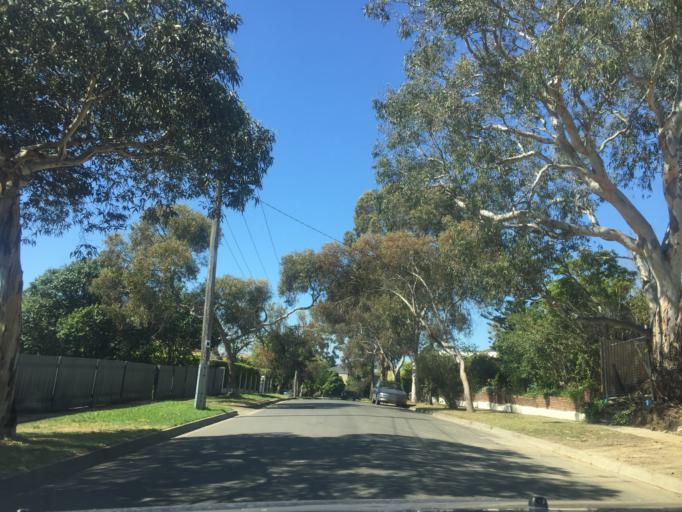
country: AU
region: Victoria
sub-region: Boroondara
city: Kew East
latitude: -37.7929
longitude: 145.0437
